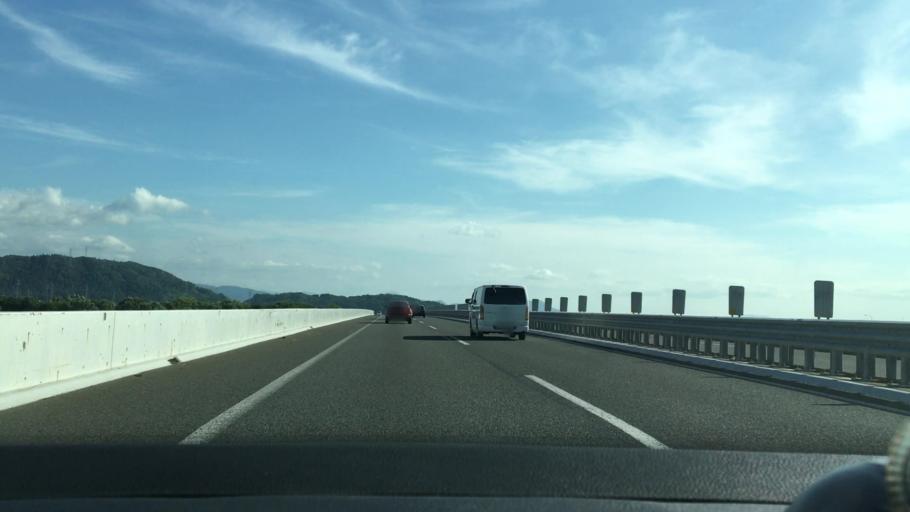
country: JP
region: Fukui
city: Maruoka
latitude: 36.1029
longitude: 136.2801
